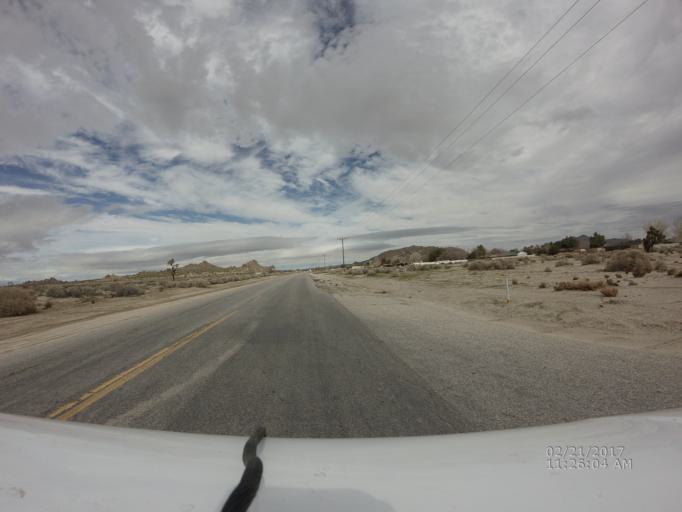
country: US
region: California
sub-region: Los Angeles County
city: Lake Los Angeles
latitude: 34.6313
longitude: -117.8628
